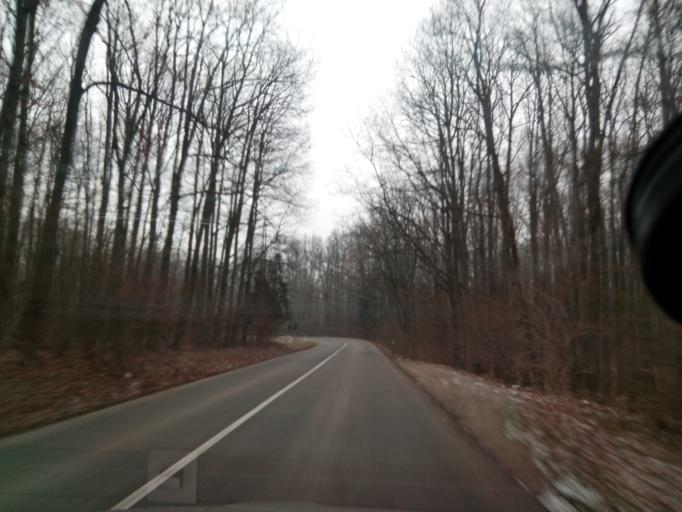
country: SK
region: Kosicky
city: Moldava nad Bodvou
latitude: 48.6882
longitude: 21.0385
